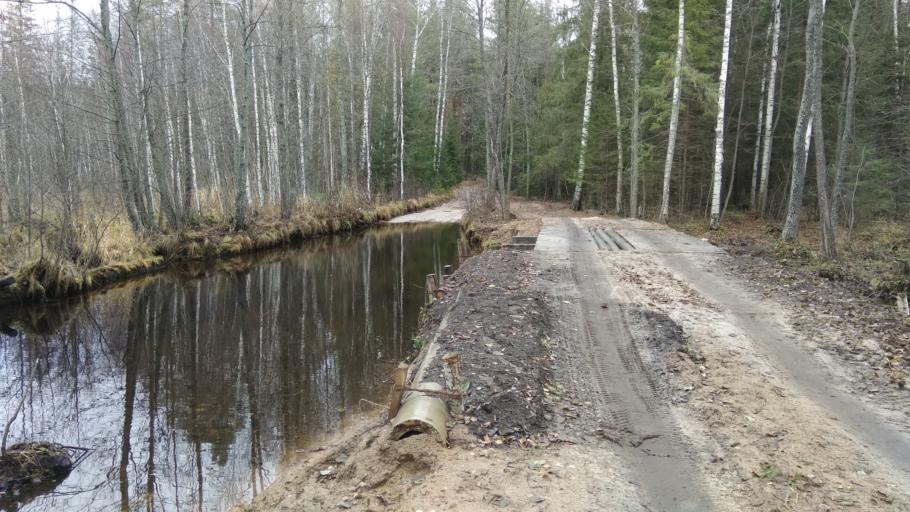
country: RU
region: Vladimir
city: Vyazniki
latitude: 56.3833
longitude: 42.2146
